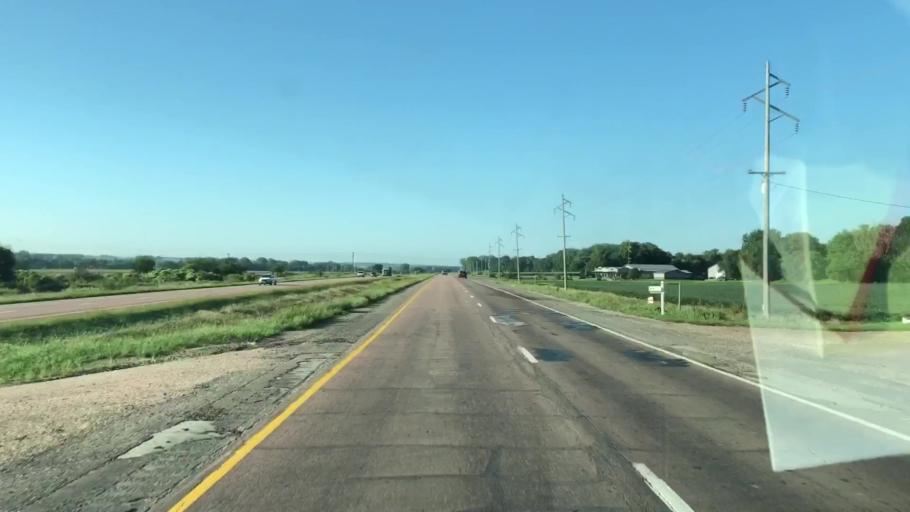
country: US
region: Iowa
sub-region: Woodbury County
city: Sioux City
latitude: 42.5976
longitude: -96.3035
